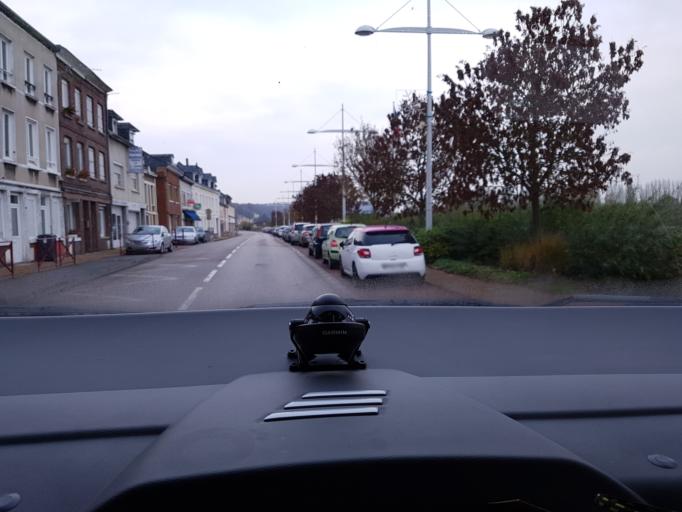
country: FR
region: Haute-Normandie
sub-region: Departement de la Seine-Maritime
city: Duclair
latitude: 49.4817
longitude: 0.8760
